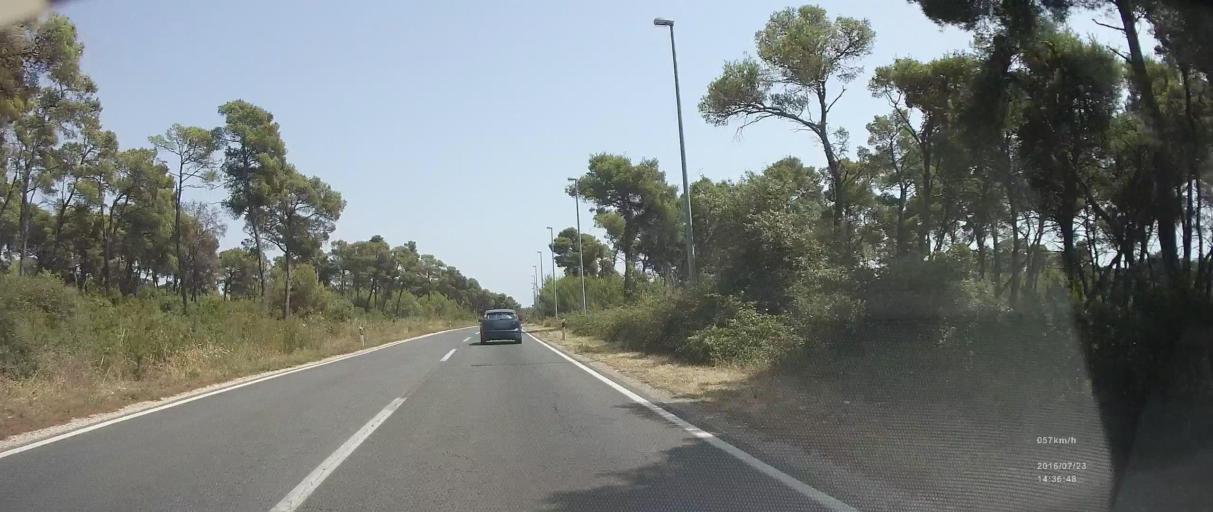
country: HR
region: Zadarska
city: Biograd na Moru
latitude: 43.9495
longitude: 15.4494
